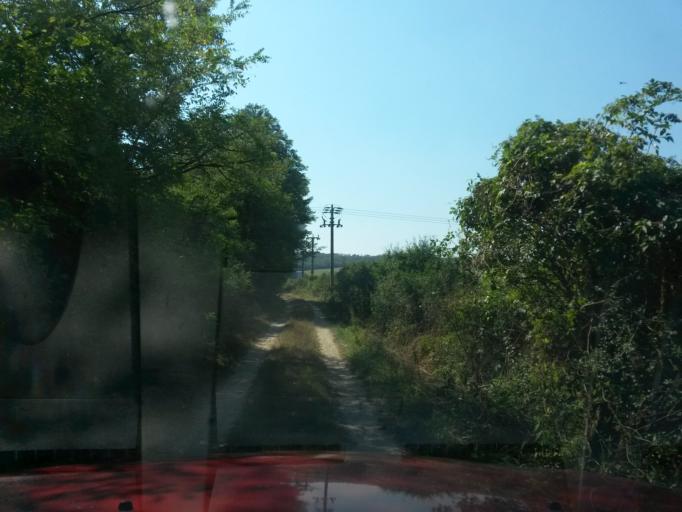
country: HU
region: Borsod-Abauj-Zemplen
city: Gonc
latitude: 48.5376
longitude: 21.1563
